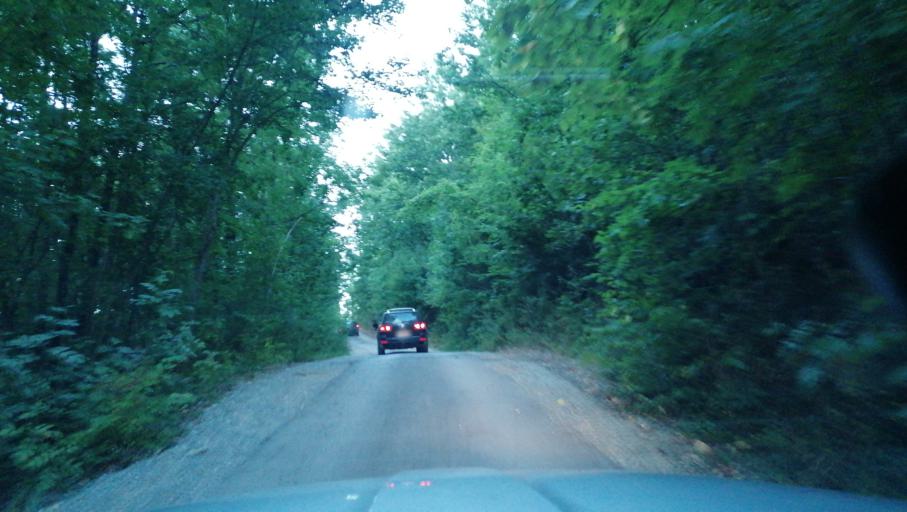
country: RS
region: Central Serbia
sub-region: Kolubarski Okrug
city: Valjevo
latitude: 44.2341
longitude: 19.8591
